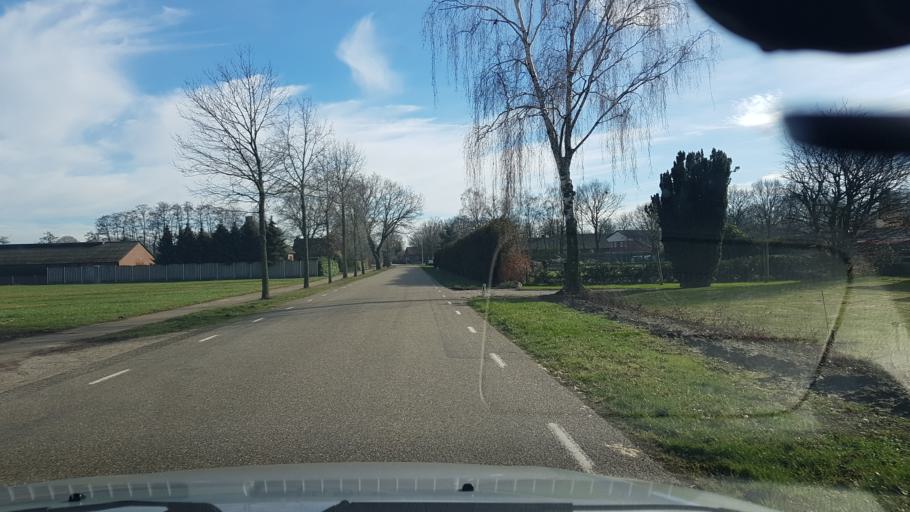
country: NL
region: Limburg
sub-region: Gemeente Nederweert
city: Nederweert
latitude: 51.2399
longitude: 5.7596
